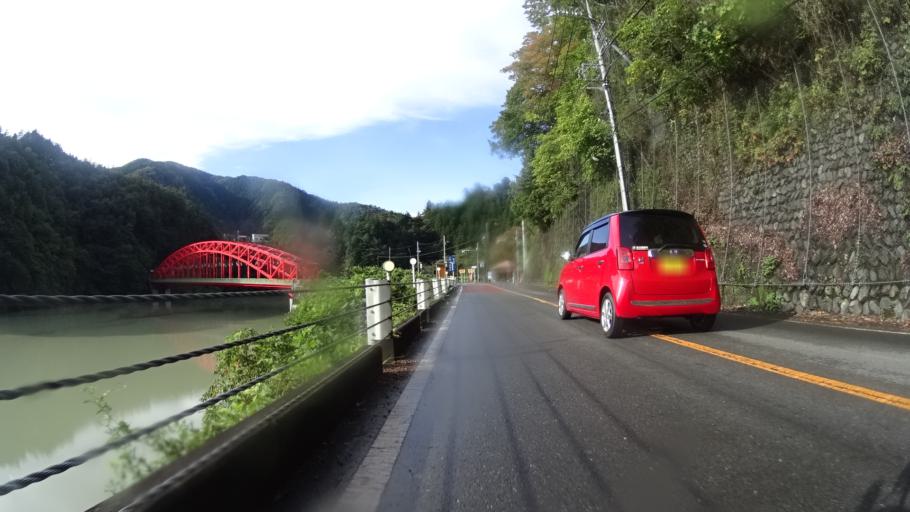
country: JP
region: Yamanashi
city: Uenohara
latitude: 35.7805
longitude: 139.0172
